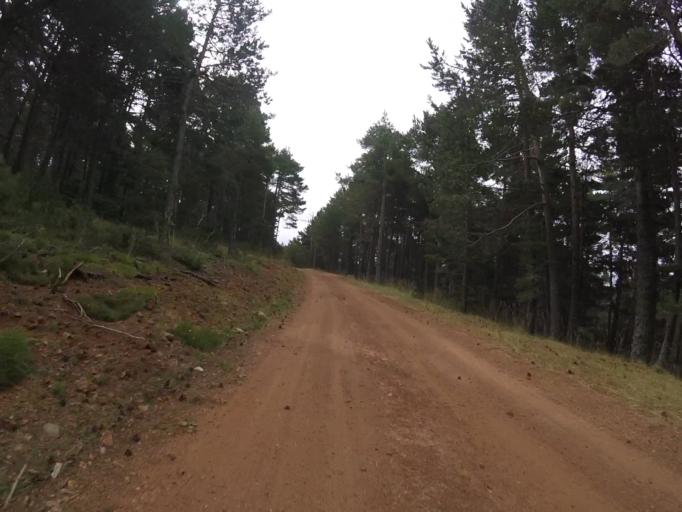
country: ES
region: Aragon
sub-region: Provincia de Teruel
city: Valdelinares
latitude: 40.3587
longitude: -0.6056
